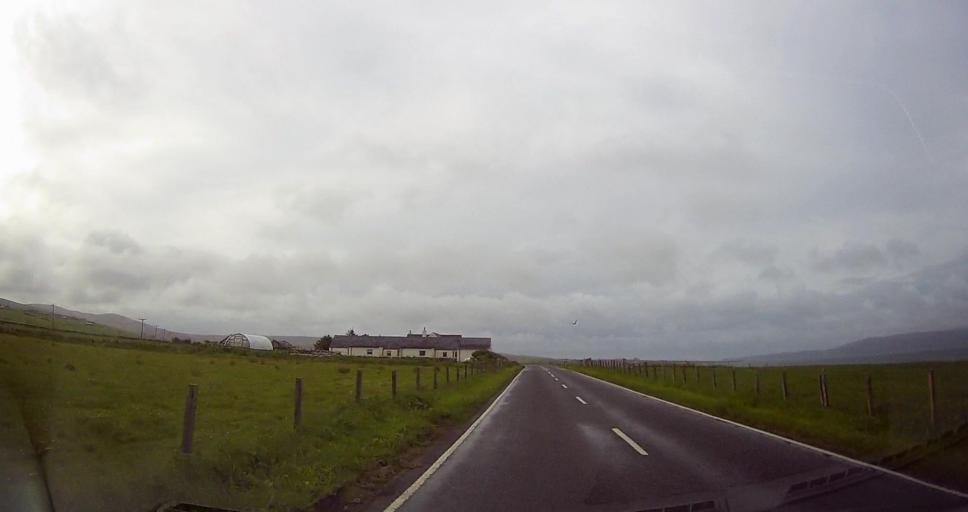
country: GB
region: Scotland
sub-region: Orkney Islands
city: Stromness
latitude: 58.9747
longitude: -3.2396
